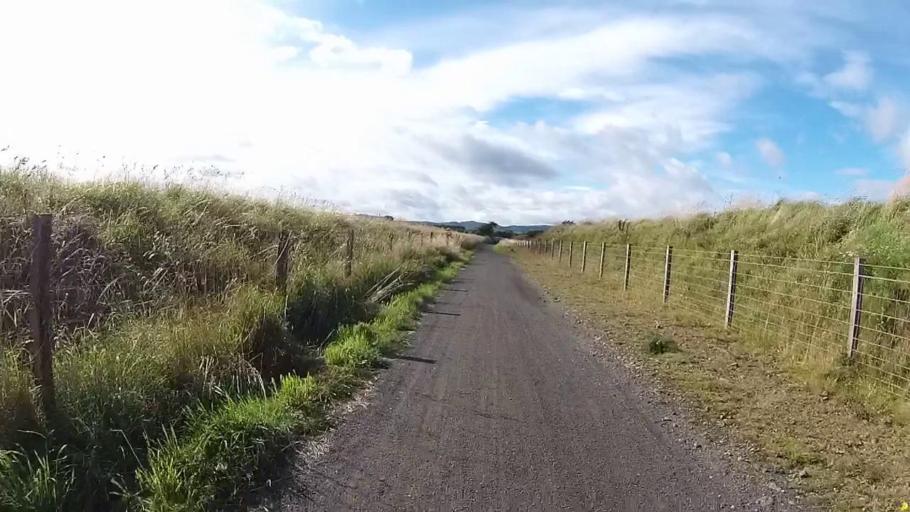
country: GB
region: Scotland
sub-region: Perth and Kinross
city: Kinross
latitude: 56.1919
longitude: -3.4111
